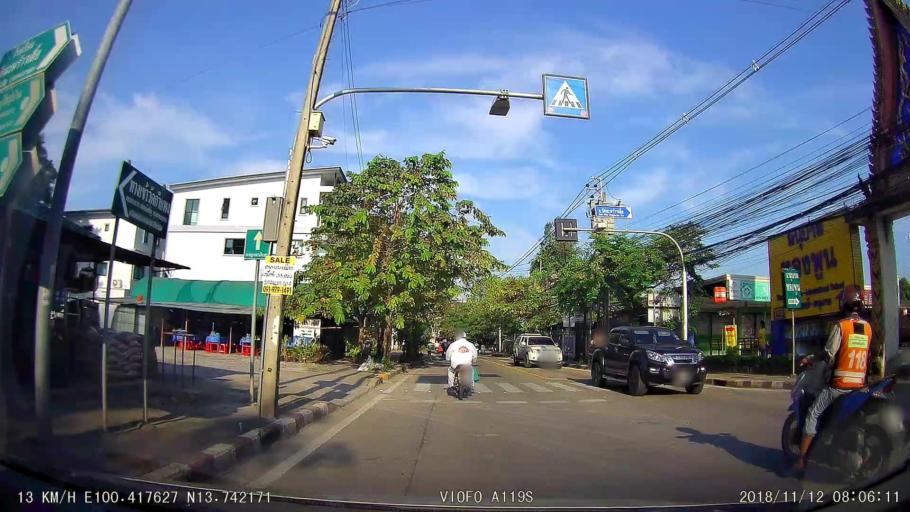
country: TH
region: Bangkok
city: Phasi Charoen
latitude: 13.7422
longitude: 100.4176
